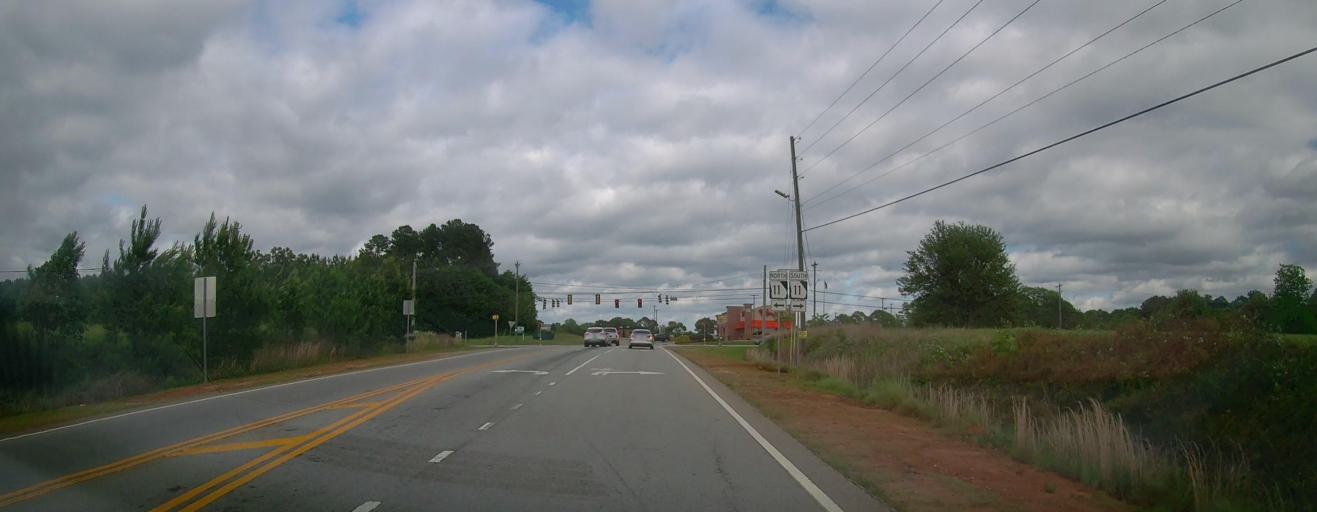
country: US
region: Georgia
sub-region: Walton County
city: Monroe
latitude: 33.8161
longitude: -83.7312
